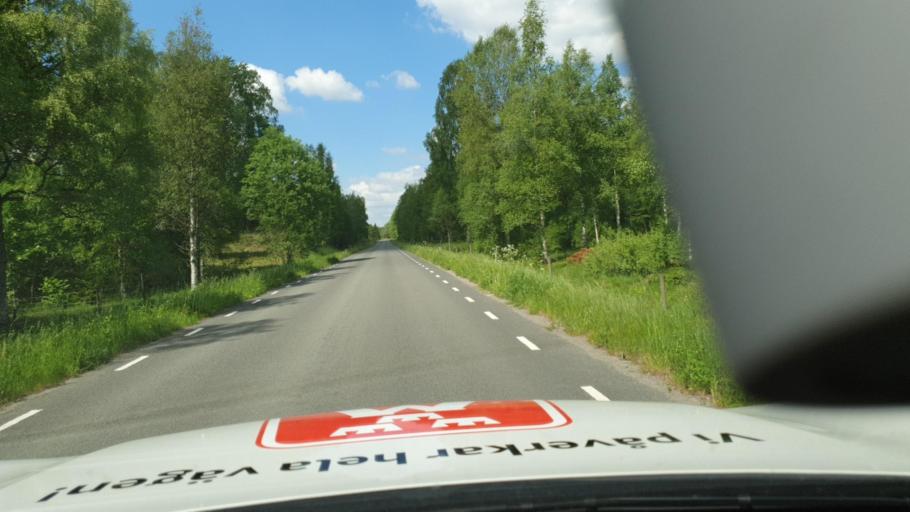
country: SE
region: Vaestra Goetaland
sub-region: Falkopings Kommun
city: Falkoeping
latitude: 58.0186
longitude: 13.6919
